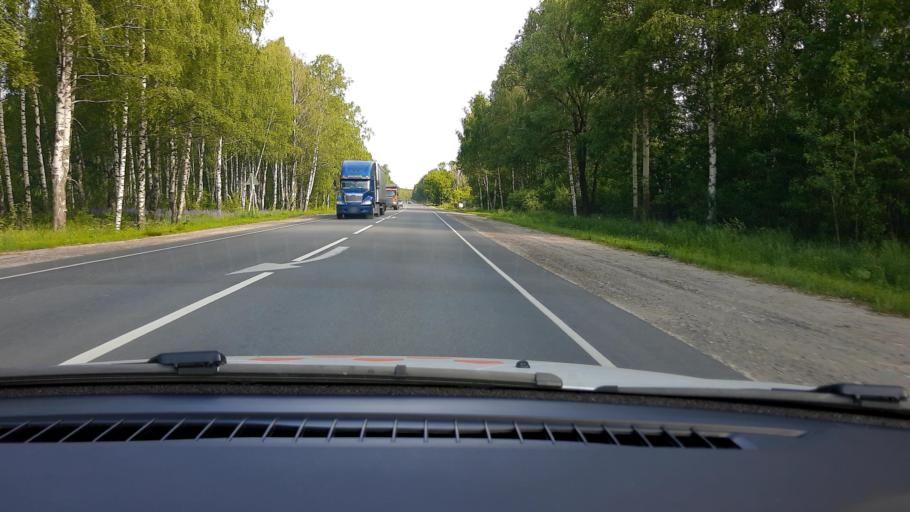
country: RU
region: Nizjnij Novgorod
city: Sitniki
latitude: 56.5290
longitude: 44.0249
